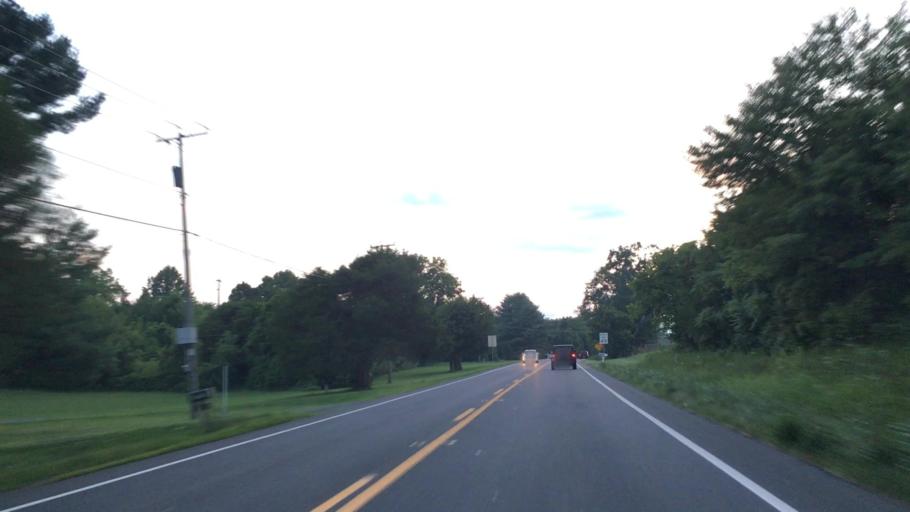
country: US
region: Virginia
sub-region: Orange County
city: Orange
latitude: 38.2437
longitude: -78.0714
